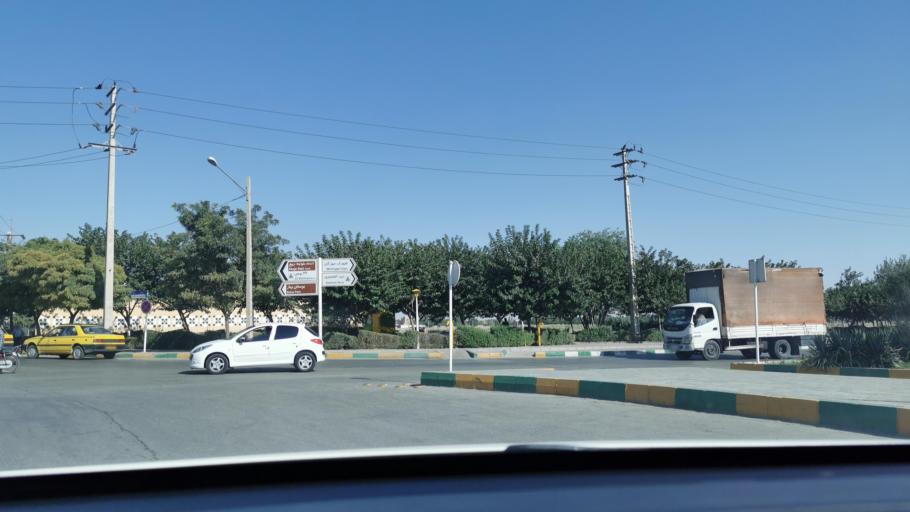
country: IR
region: Razavi Khorasan
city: Mashhad
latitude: 36.3300
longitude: 59.6464
